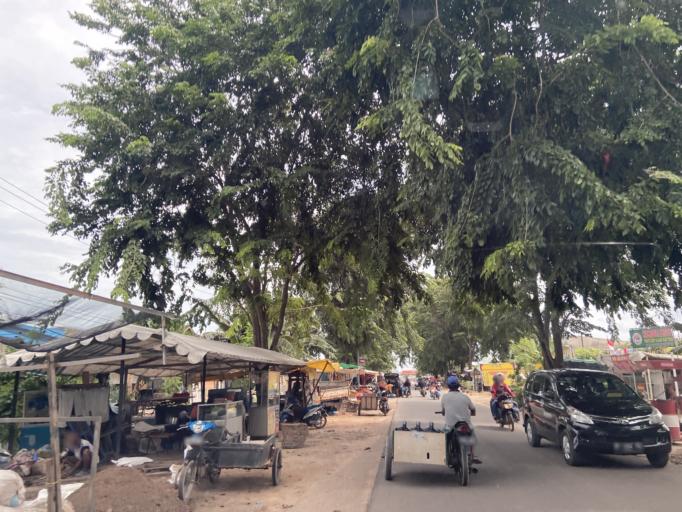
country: SG
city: Singapore
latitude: 1.0349
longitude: 103.9765
